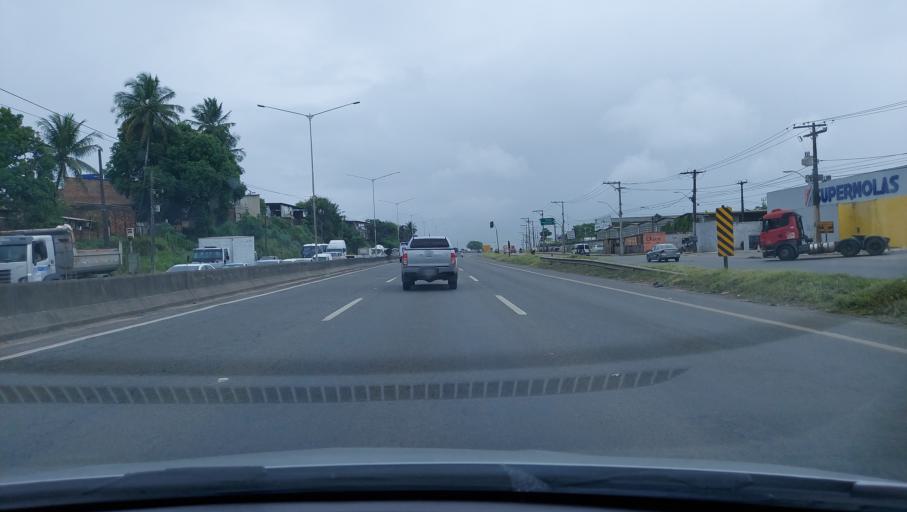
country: BR
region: Bahia
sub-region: Salvador
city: Salvador
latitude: -12.8940
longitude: -38.4473
